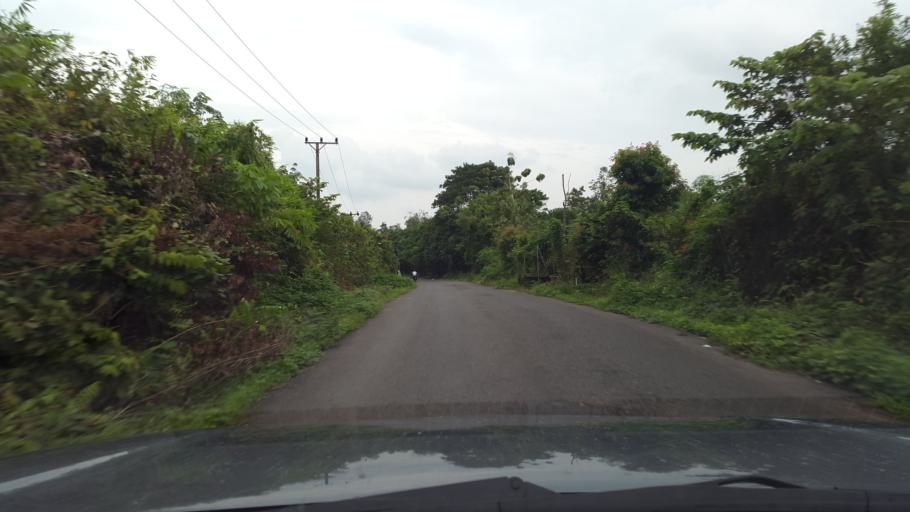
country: ID
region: South Sumatra
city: Gunungmenang
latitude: -3.1693
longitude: 104.0037
